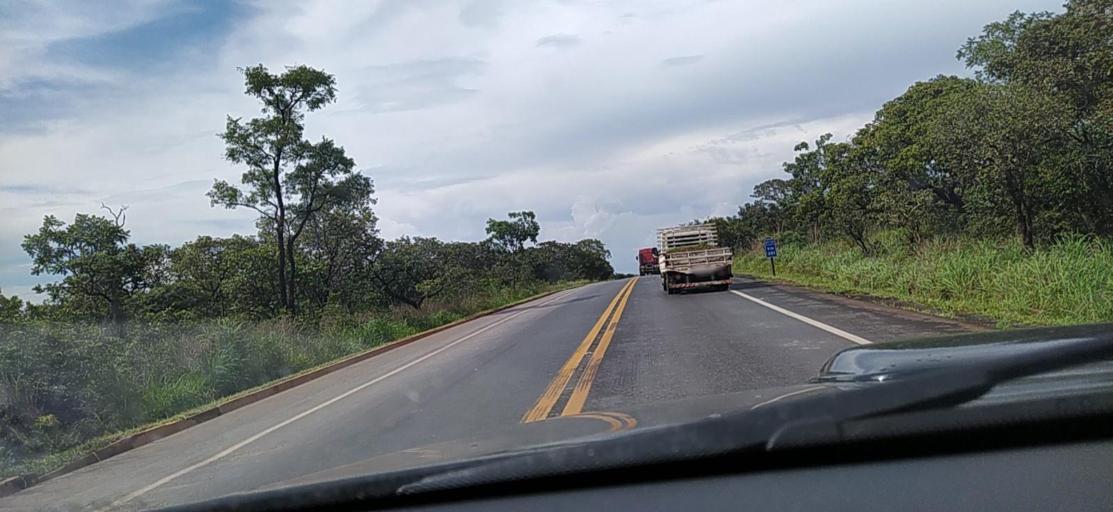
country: BR
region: Minas Gerais
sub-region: Montes Claros
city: Montes Claros
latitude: -16.8644
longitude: -43.8538
